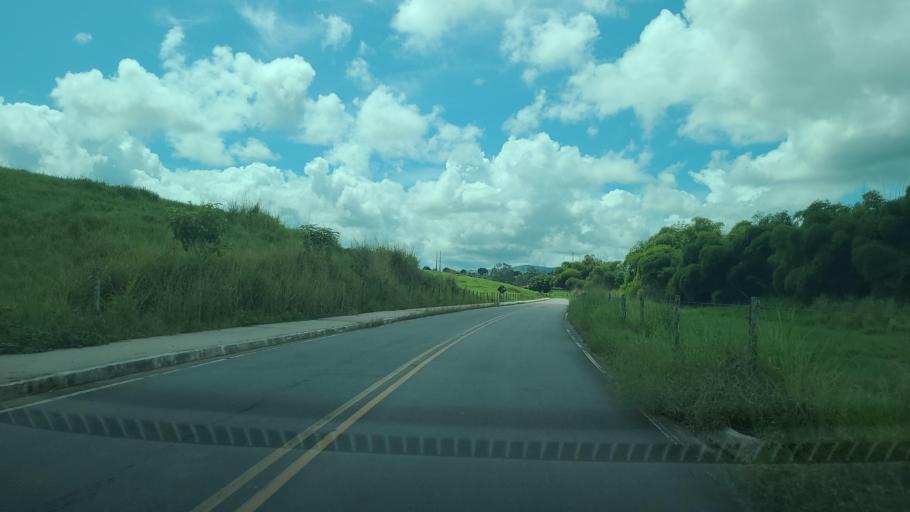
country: BR
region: Alagoas
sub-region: Uniao Dos Palmares
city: Uniao dos Palmares
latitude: -9.1577
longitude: -36.0429
